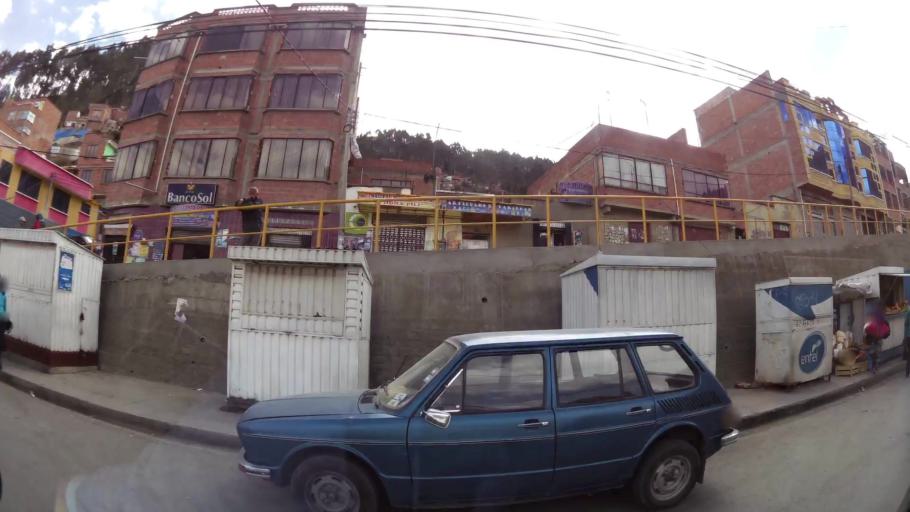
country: BO
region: La Paz
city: La Paz
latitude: -16.4657
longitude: -68.1190
